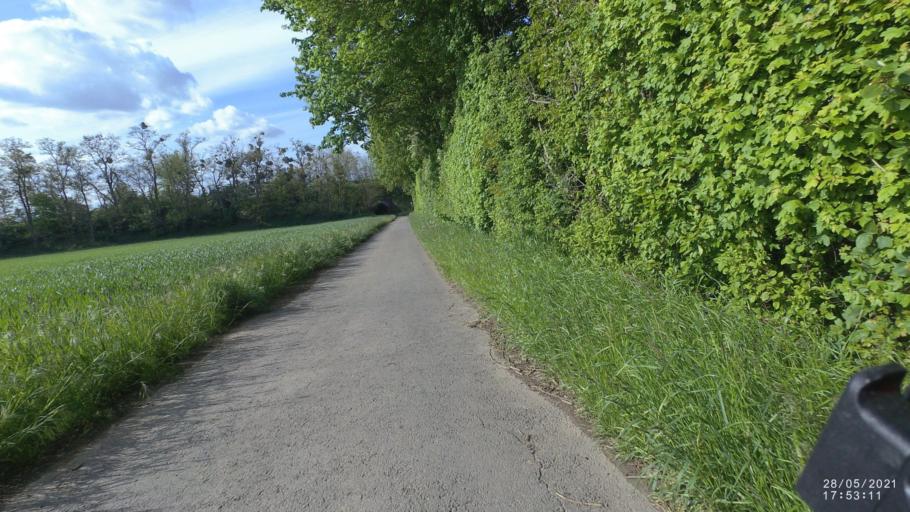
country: DE
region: Rheinland-Pfalz
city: Munstermaifeld
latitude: 50.2483
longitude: 7.3488
